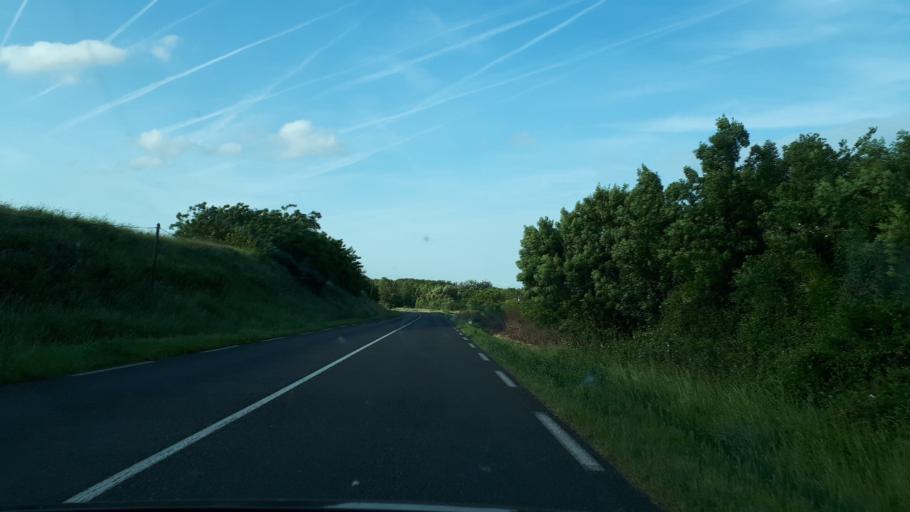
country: FR
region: Centre
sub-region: Departement d'Indre-et-Loire
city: Villedomer
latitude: 47.5714
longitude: 0.8935
